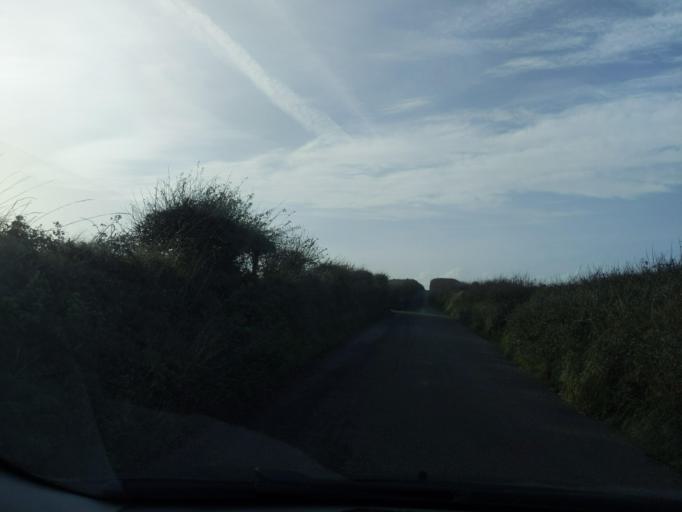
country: GB
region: England
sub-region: Cornwall
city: Pillaton
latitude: 50.3640
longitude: -4.3229
